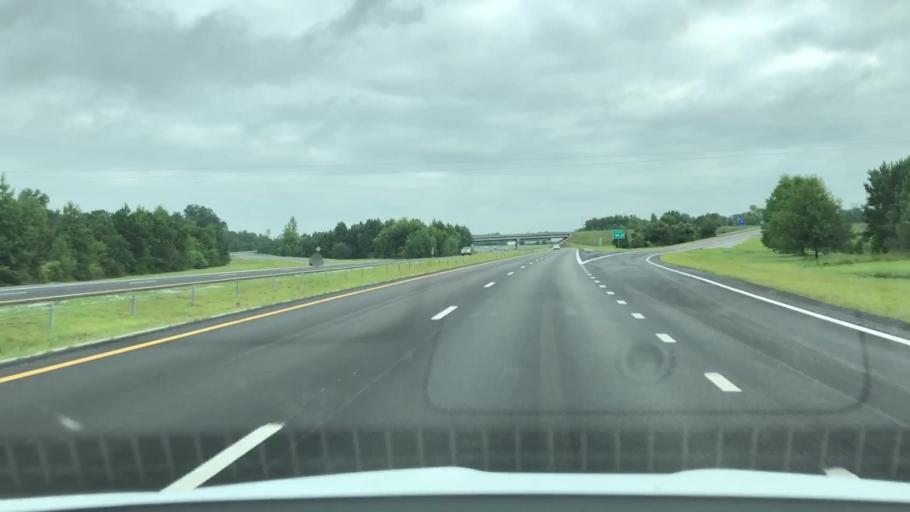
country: US
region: North Carolina
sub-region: Wayne County
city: Fremont
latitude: 35.5455
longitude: -77.9889
